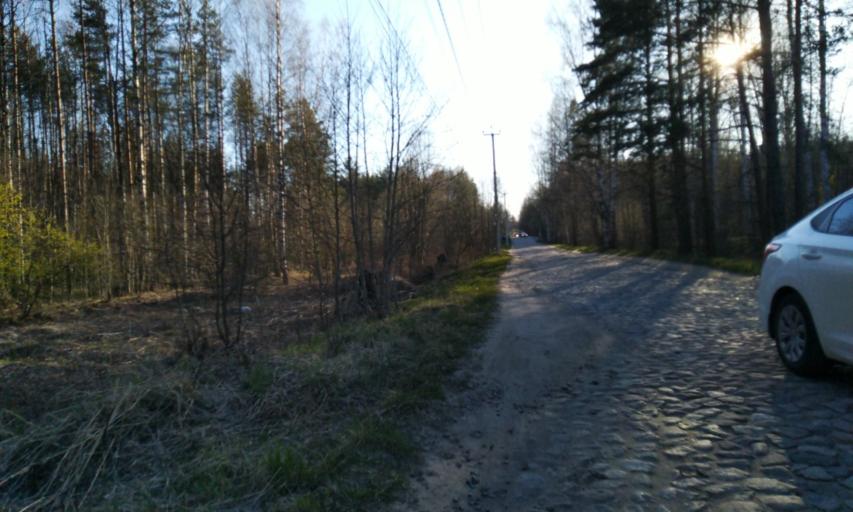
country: RU
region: Leningrad
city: Toksovo
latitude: 60.1394
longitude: 30.5560
